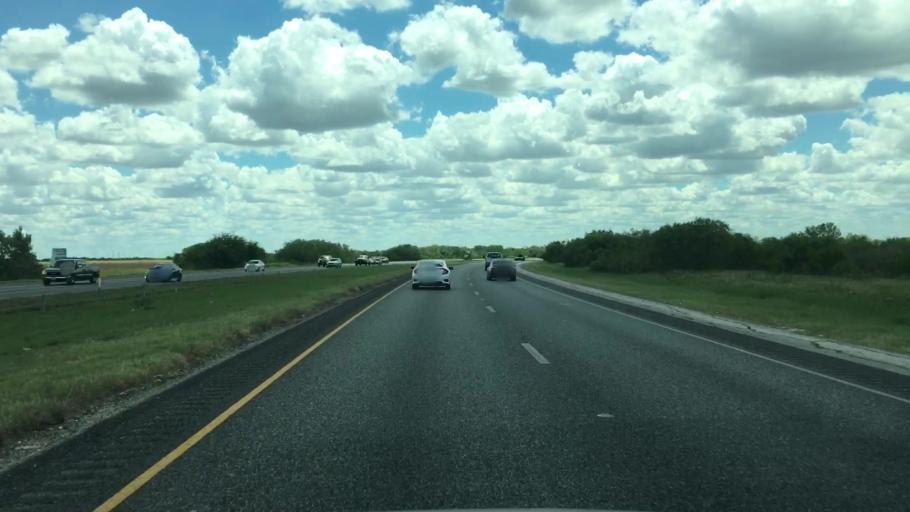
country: US
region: Texas
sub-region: Bexar County
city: Elmendorf
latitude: 29.3011
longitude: -98.3957
